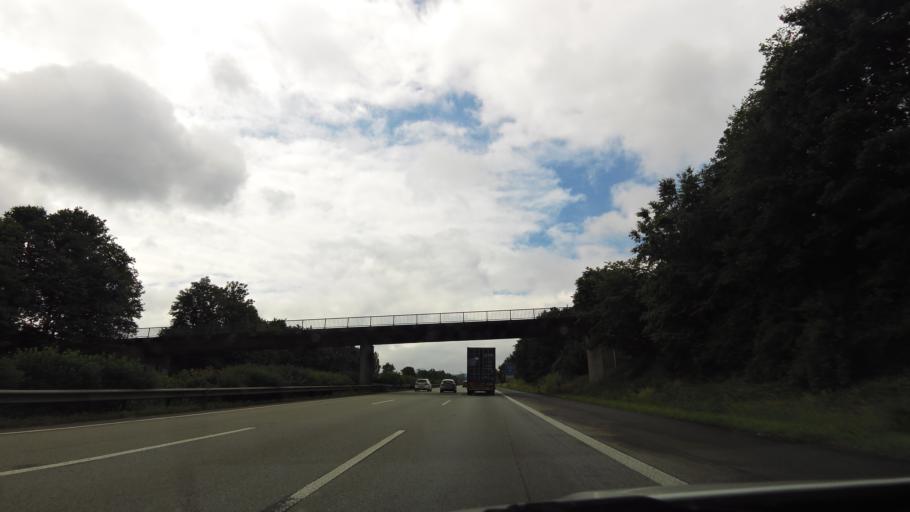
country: DE
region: Rheinland-Pfalz
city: Niederzissen
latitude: 50.4505
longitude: 7.2302
